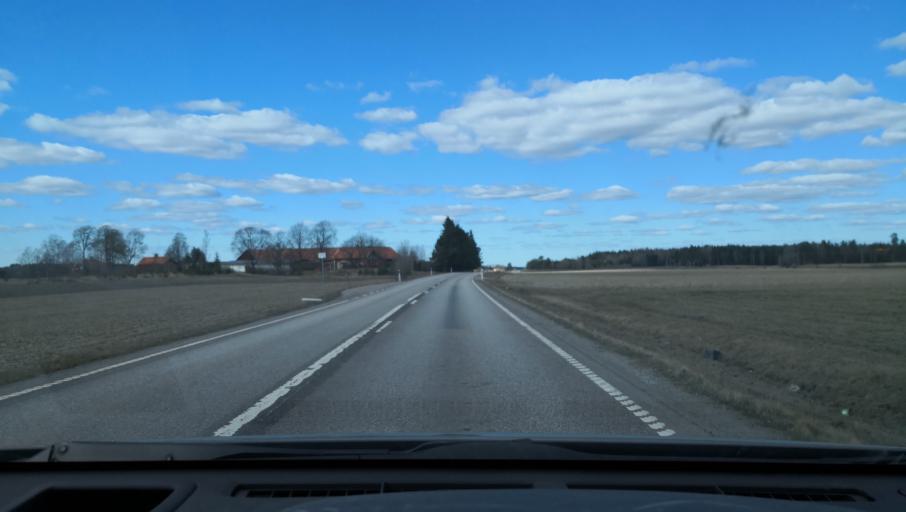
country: SE
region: Vaestmanland
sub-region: Sala Kommun
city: Sala
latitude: 59.8635
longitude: 16.6307
